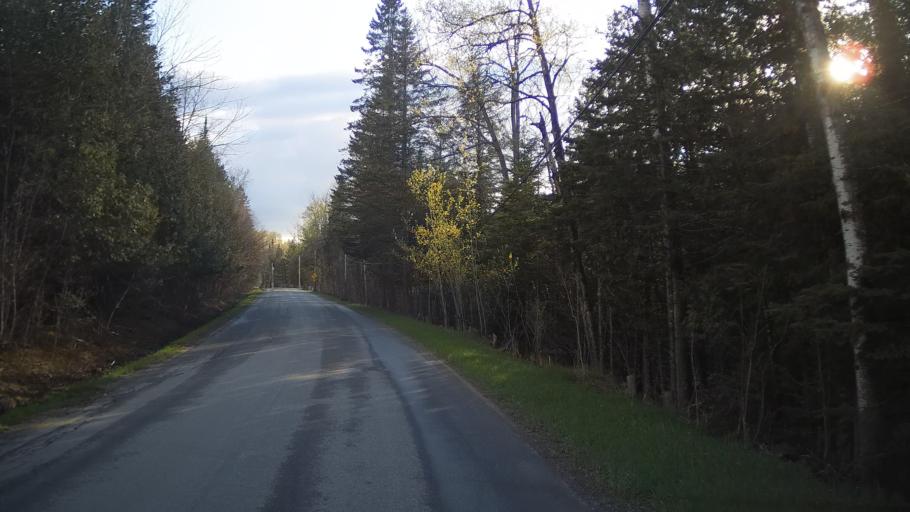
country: US
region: Vermont
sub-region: Orleans County
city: Newport
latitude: 44.7402
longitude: -72.2112
